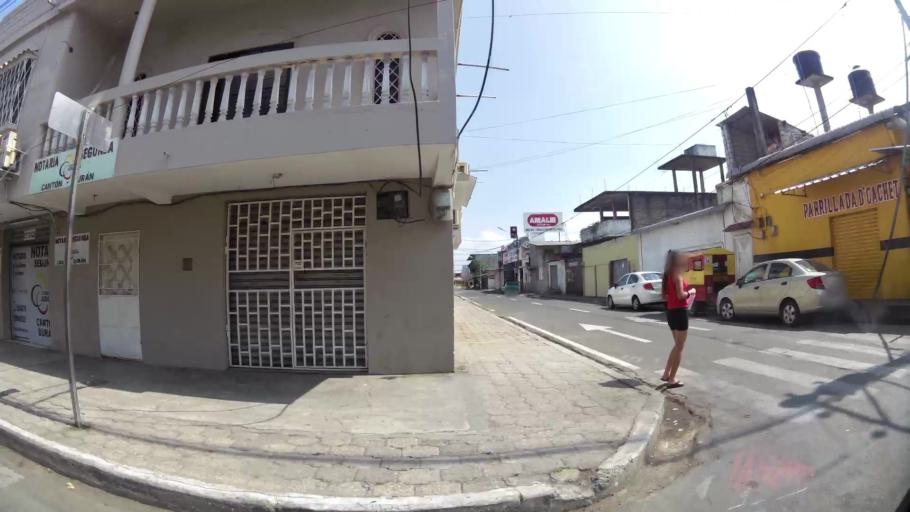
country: EC
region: Guayas
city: Eloy Alfaro
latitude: -2.1589
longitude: -79.8397
